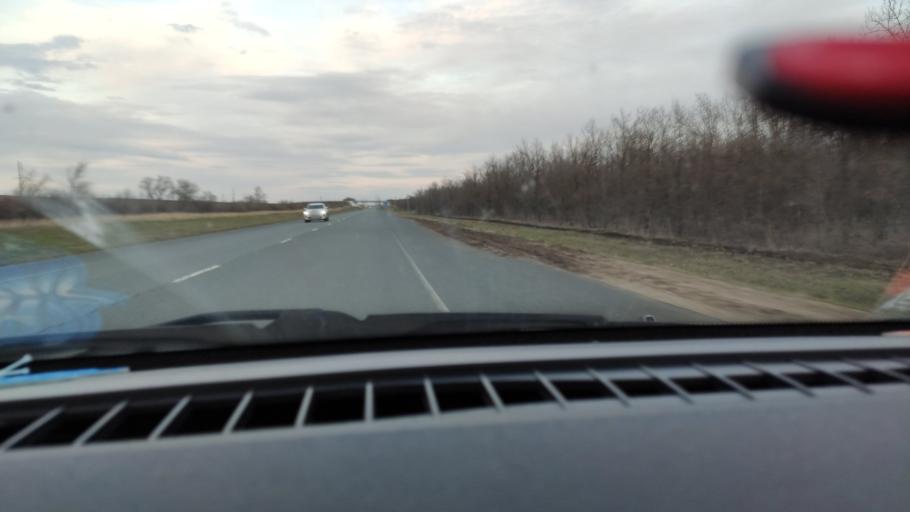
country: RU
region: Saratov
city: Yelshanka
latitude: 51.8260
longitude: 46.2873
